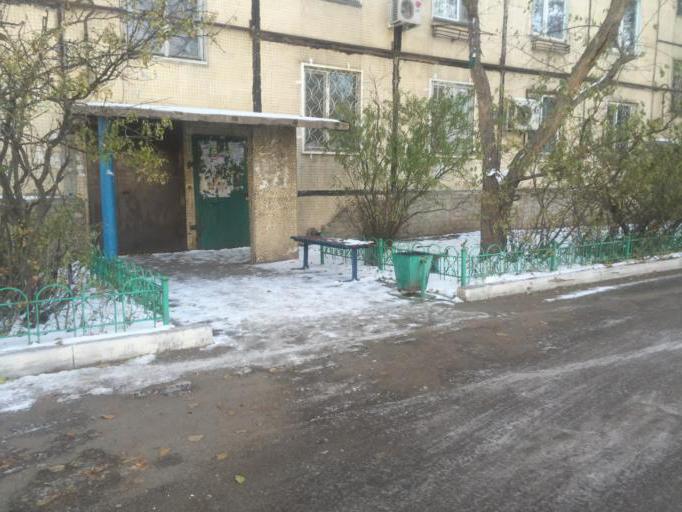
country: KZ
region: Astana Qalasy
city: Astana
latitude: 51.1875
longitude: 71.4145
